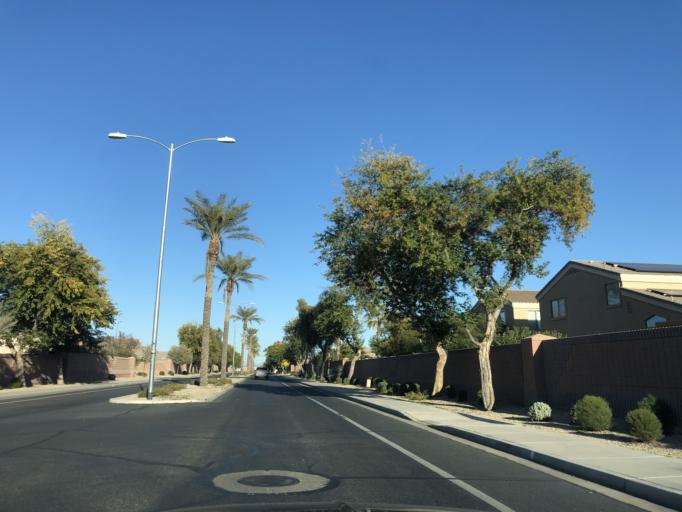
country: US
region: Arizona
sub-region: Maricopa County
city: El Mirage
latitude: 33.6170
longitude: -112.3319
